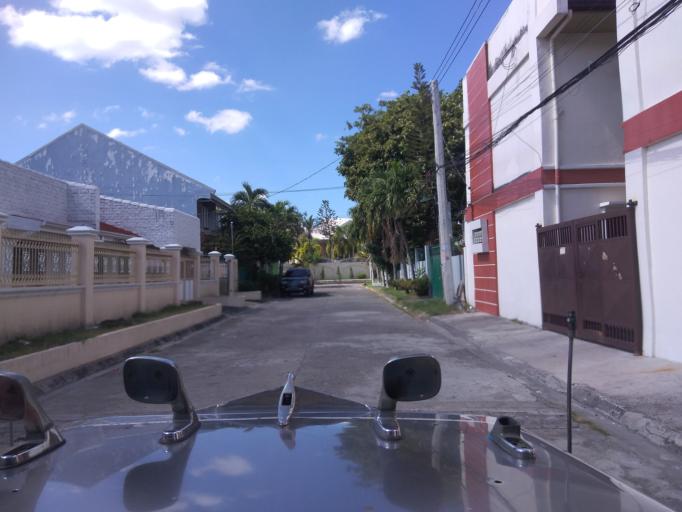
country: PH
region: Central Luzon
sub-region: Province of Pampanga
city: Calibutbut
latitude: 15.1154
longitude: 120.6009
